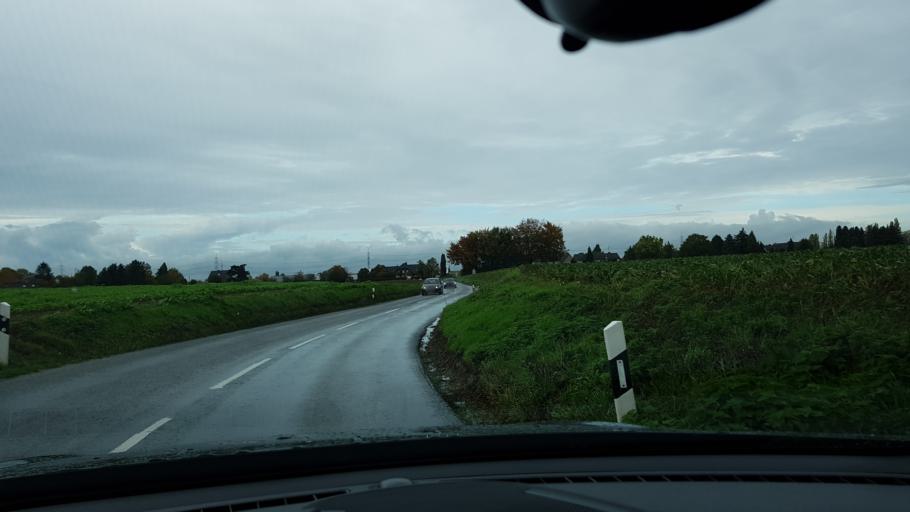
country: DE
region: North Rhine-Westphalia
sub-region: Regierungsbezirk Dusseldorf
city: Rommerskirchen
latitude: 51.0700
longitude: 6.6803
